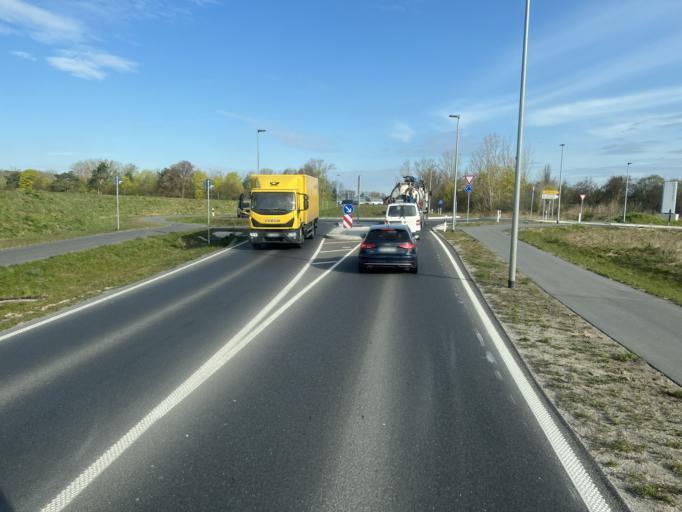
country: DE
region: Brandenburg
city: Stahnsdorf
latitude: 52.3855
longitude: 13.2298
